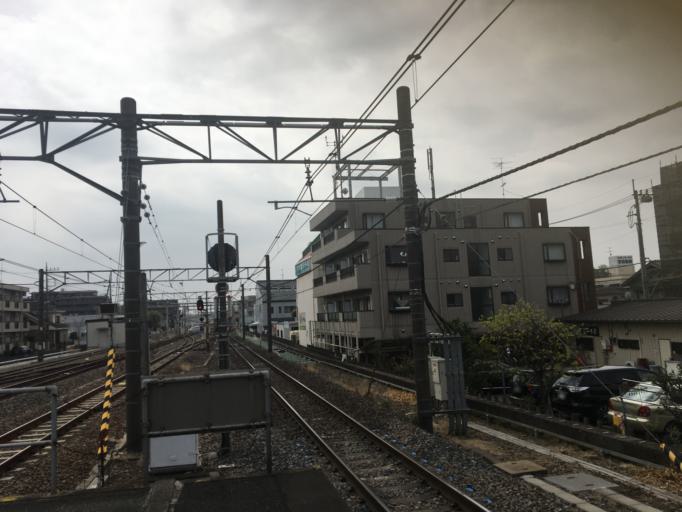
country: JP
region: Saitama
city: Okegawa
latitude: 36.0306
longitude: 139.5345
